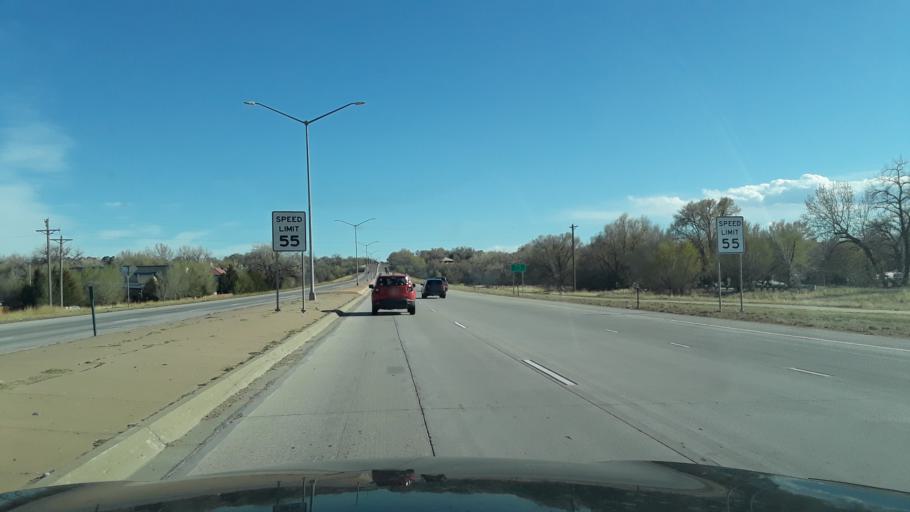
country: US
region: Colorado
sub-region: Pueblo County
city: Pueblo
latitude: 38.2747
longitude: -104.6627
